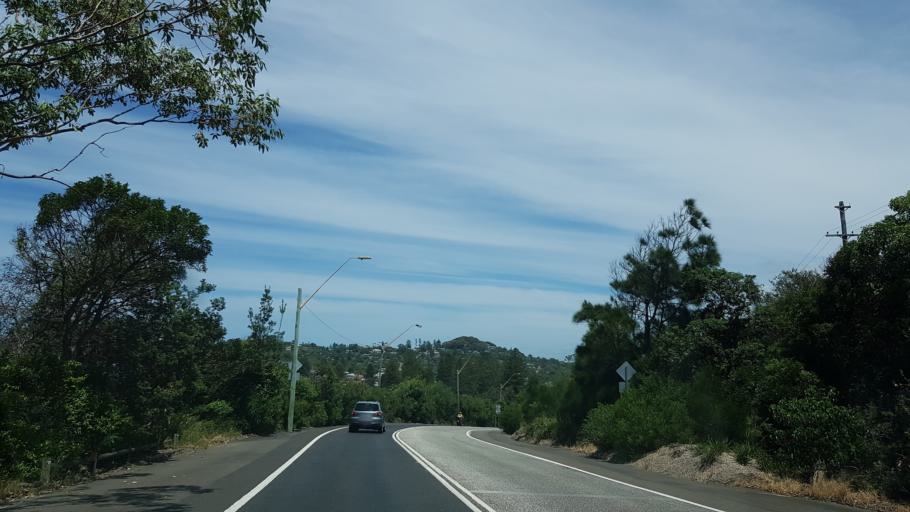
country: AU
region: New South Wales
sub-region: Pittwater
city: Bilgola Beach
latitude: -33.6489
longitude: 151.3246
